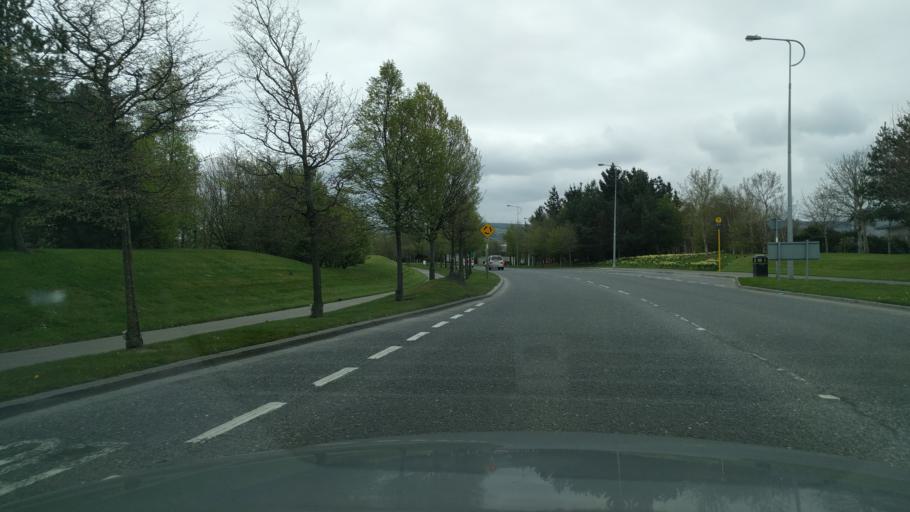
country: IE
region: Leinster
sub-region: South Dublin
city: Saggart
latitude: 53.2912
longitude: -6.4271
